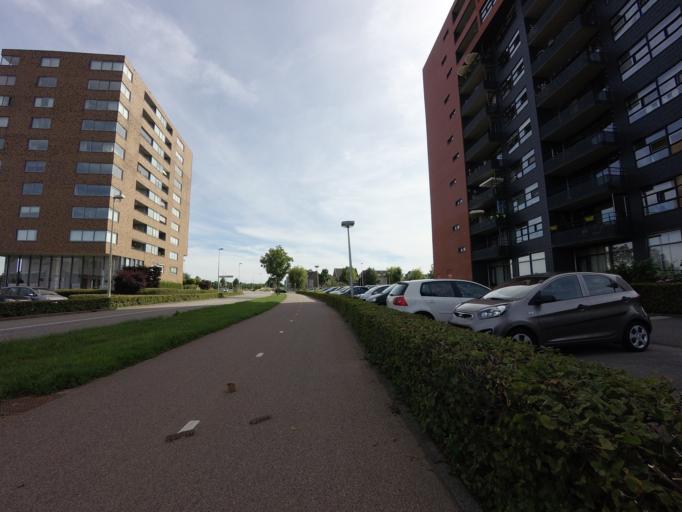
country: NL
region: Utrecht
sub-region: Stichtse Vecht
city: Maarssen
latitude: 52.0867
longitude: 5.0492
